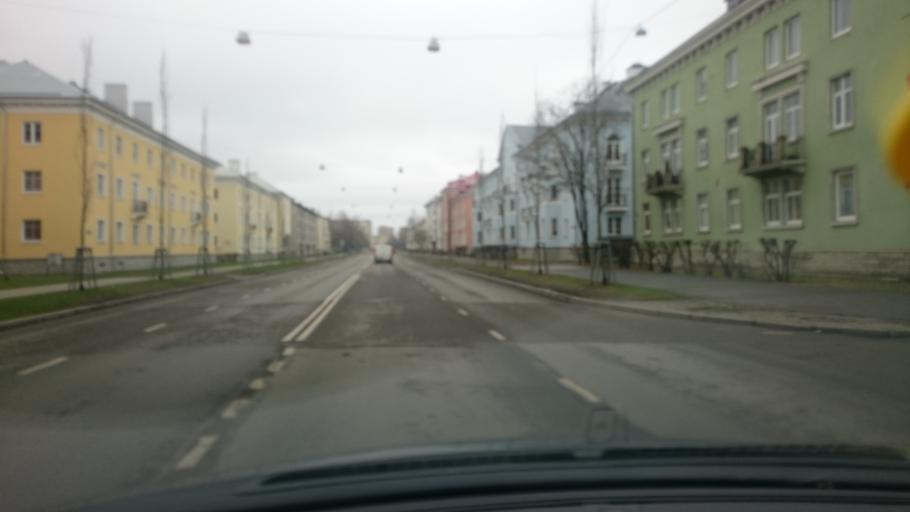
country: EE
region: Harju
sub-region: Tallinna linn
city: Tallinn
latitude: 59.4536
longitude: 24.6915
